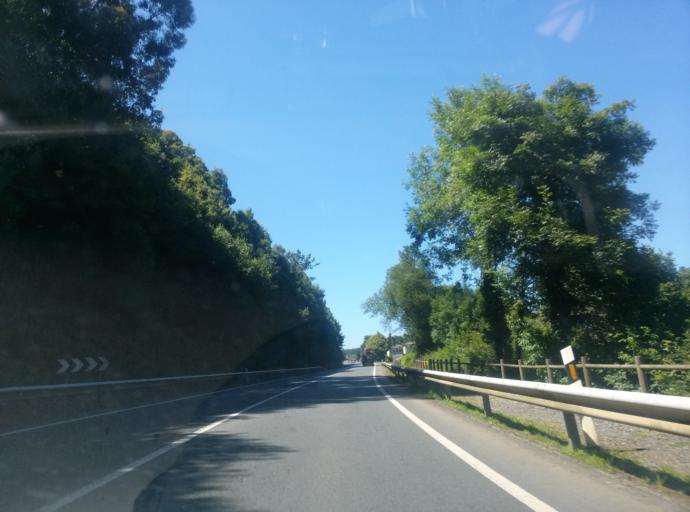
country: ES
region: Galicia
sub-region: Provincia de Lugo
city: Meira
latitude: 43.2165
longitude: -7.3123
